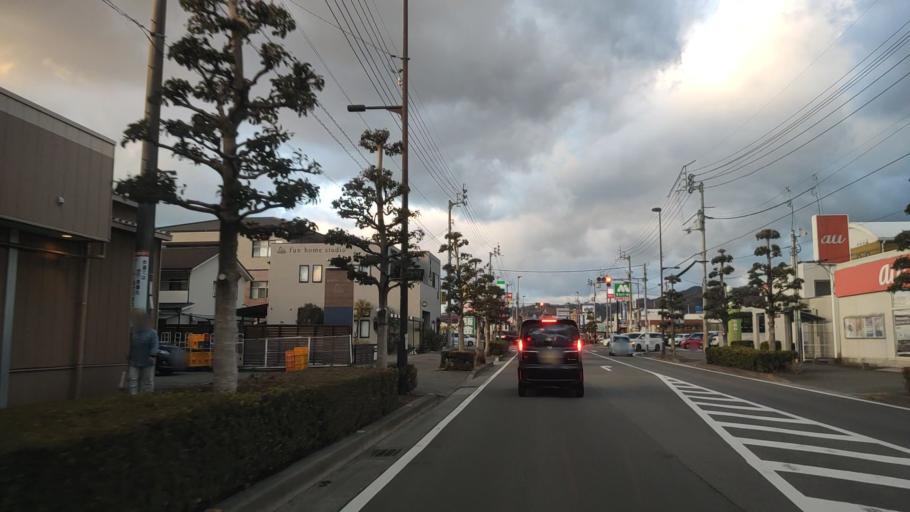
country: JP
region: Ehime
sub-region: Shikoku-chuo Shi
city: Matsuyama
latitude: 33.8322
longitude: 132.7873
